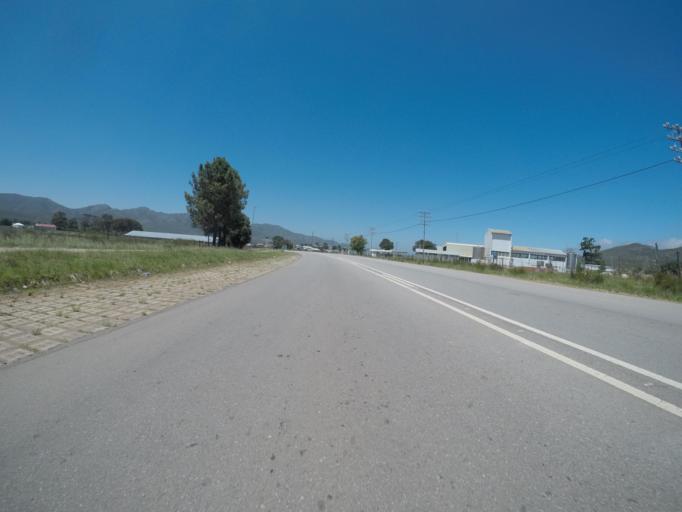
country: ZA
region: Eastern Cape
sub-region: Cacadu District Municipality
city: Kareedouw
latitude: -33.9526
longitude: 24.2976
